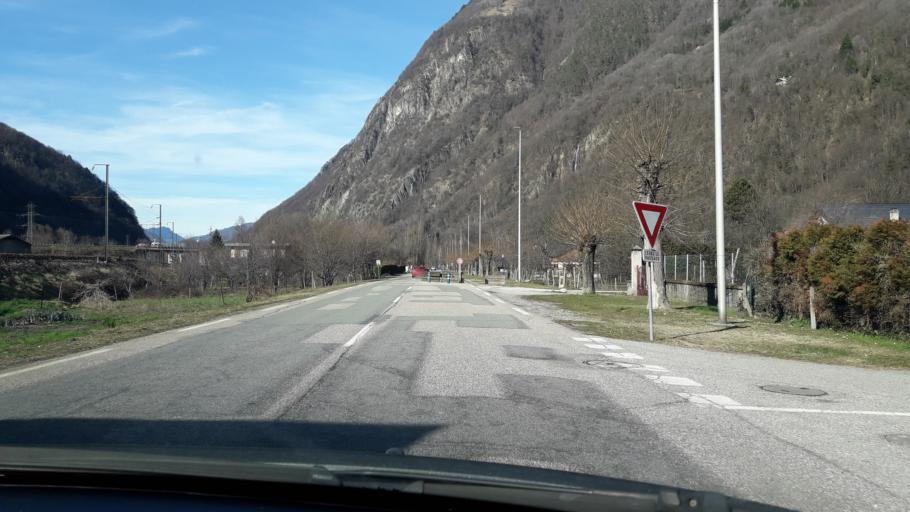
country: FR
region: Rhone-Alpes
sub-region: Departement de la Savoie
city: Aigueblanche
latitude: 45.5590
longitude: 6.4690
